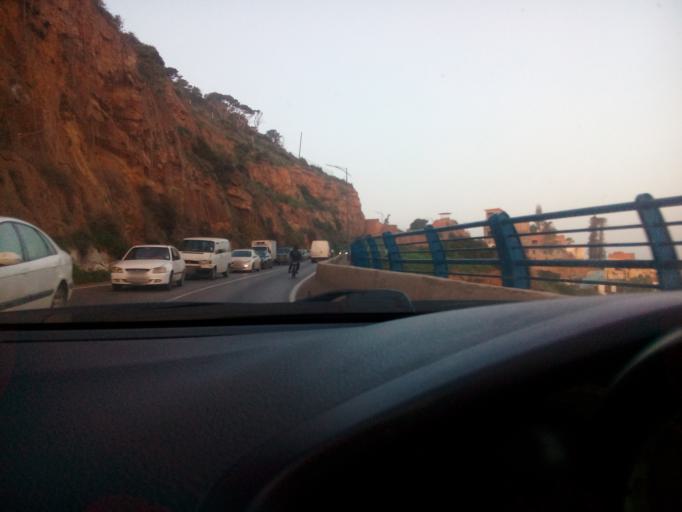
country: DZ
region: Oran
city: Oran
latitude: 35.7131
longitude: -0.6610
